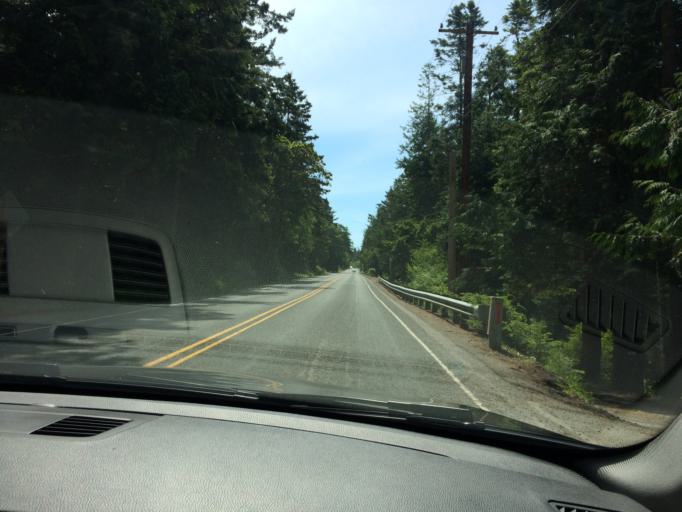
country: US
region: Washington
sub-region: Skagit County
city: Anacortes
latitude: 48.4732
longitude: -122.6553
